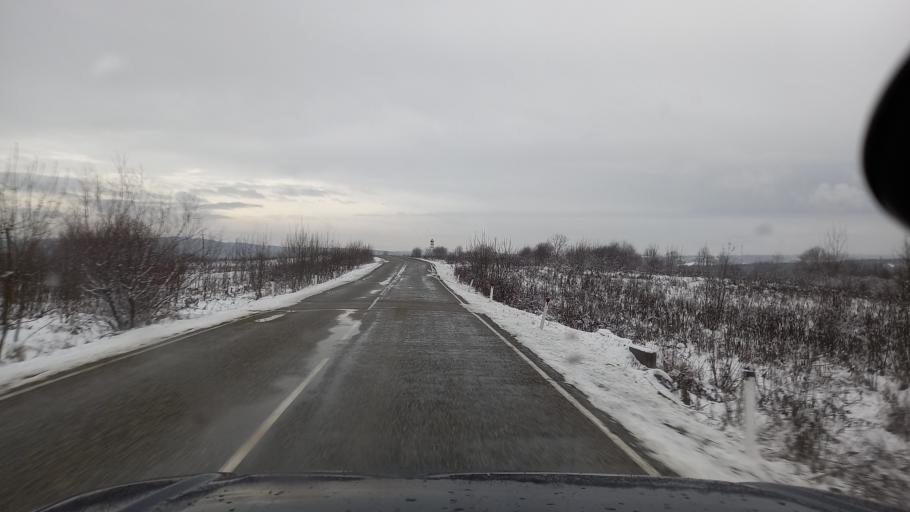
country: RU
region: Adygeya
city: Abadzekhskaya
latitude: 44.3586
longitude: 40.3802
